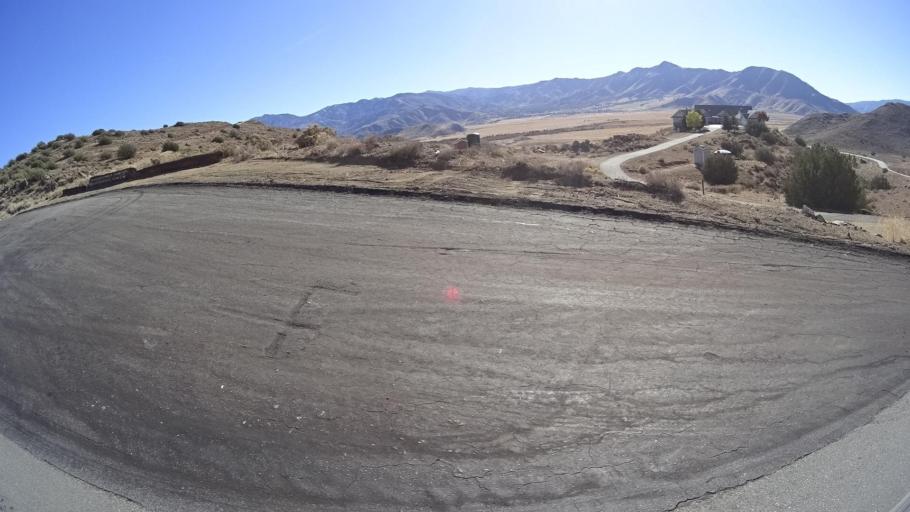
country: US
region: California
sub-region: Kern County
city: Wofford Heights
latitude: 35.6824
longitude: -118.3900
